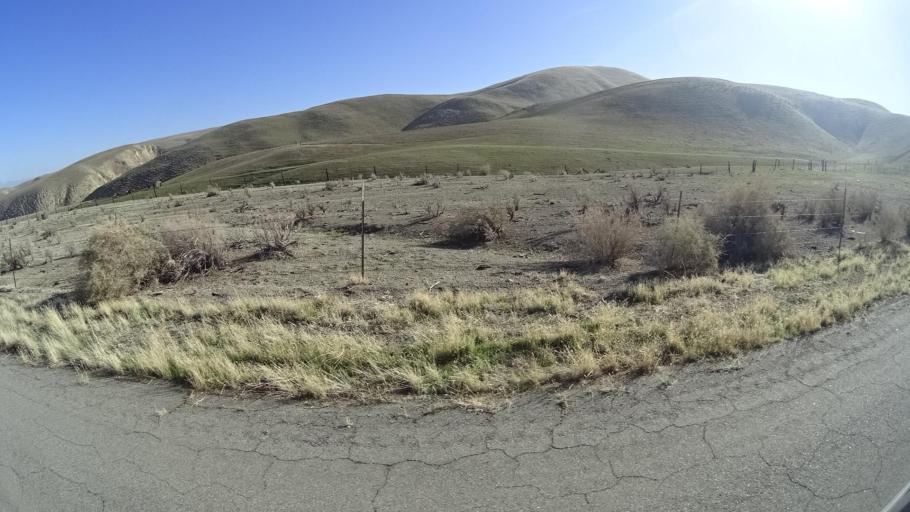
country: US
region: California
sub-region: Kern County
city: Maricopa
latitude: 34.9838
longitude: -119.3970
